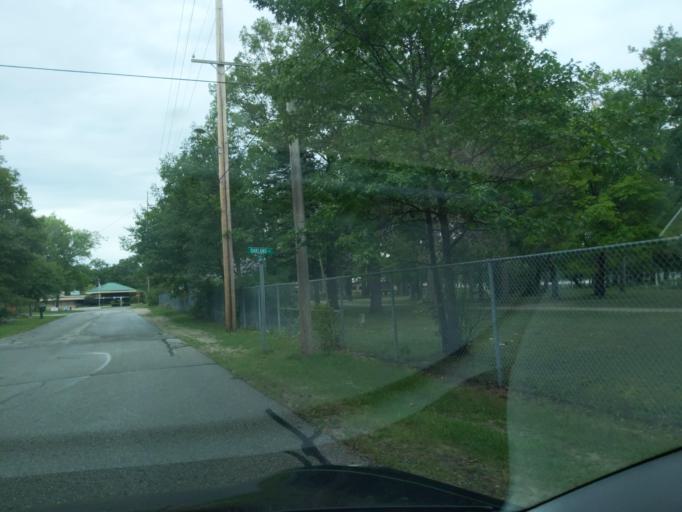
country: US
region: Michigan
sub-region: Grand Traverse County
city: Traverse City
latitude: 44.7574
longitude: -85.5903
